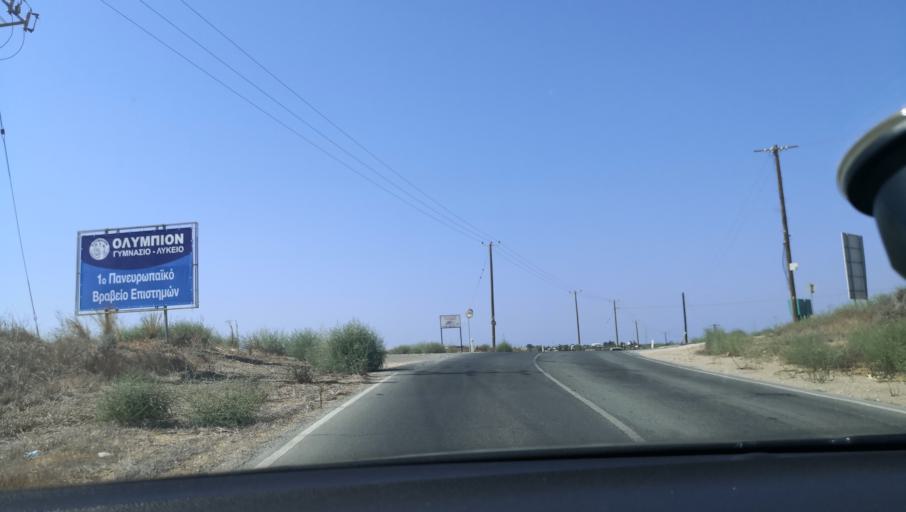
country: CY
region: Lefkosia
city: Kato Deftera
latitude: 35.1210
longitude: 33.2592
